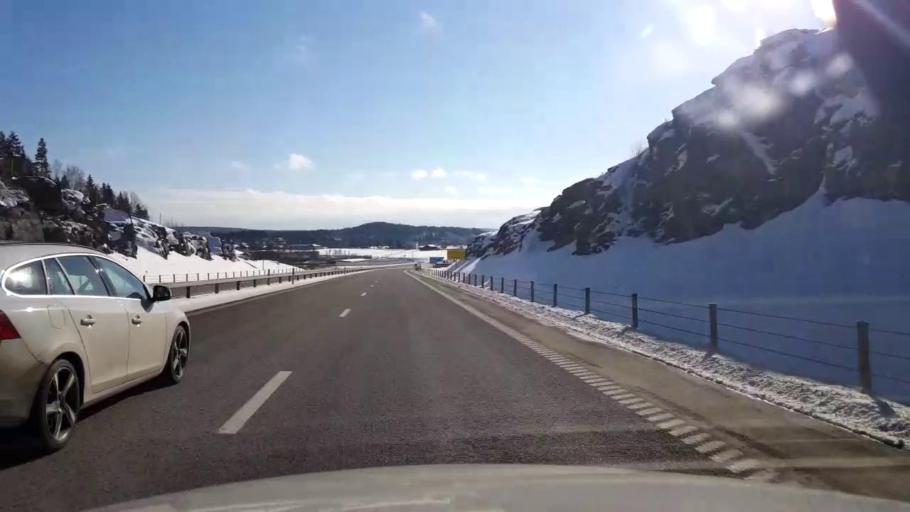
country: SE
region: Vaesternorrland
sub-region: Sundsvalls Kommun
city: Nolby
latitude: 62.2999
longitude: 17.3465
